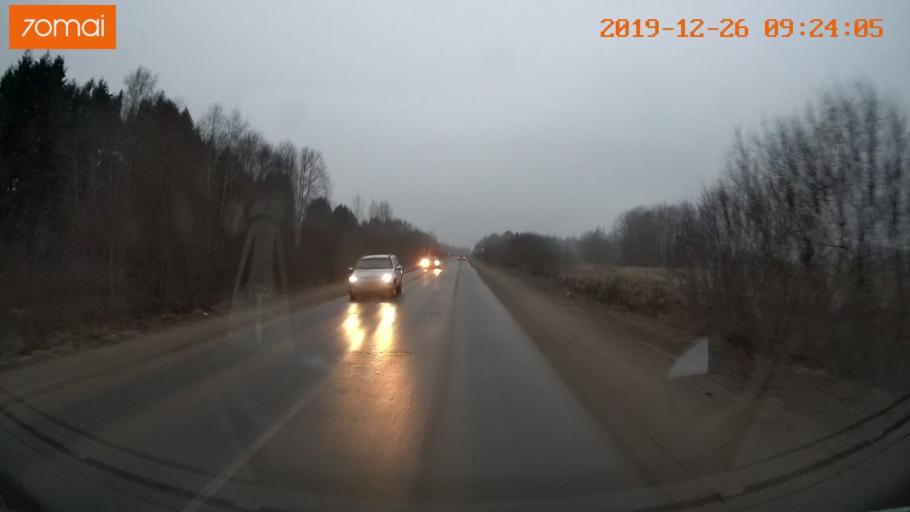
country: RU
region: Vologda
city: Gryazovets
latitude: 58.9965
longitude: 40.2026
